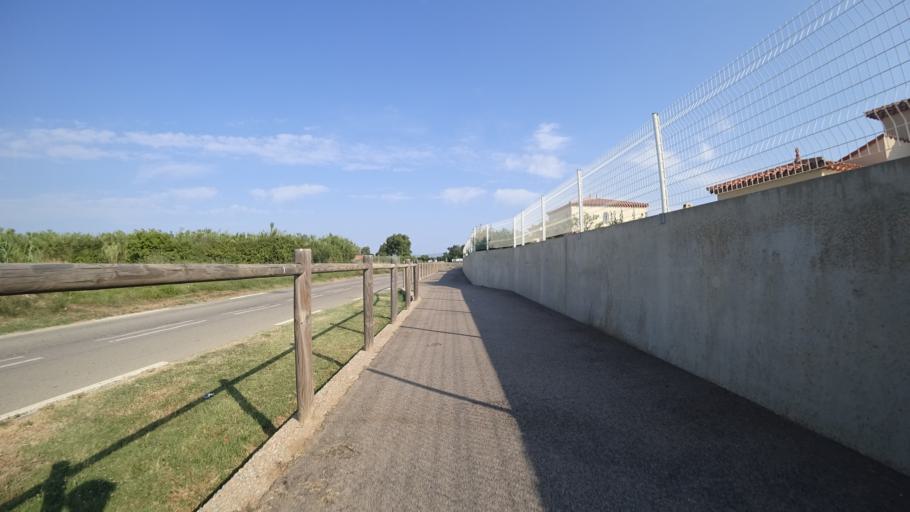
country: FR
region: Languedoc-Roussillon
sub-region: Departement des Pyrenees-Orientales
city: Saint-Laurent-de-la-Salanque
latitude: 42.7693
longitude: 2.9788
